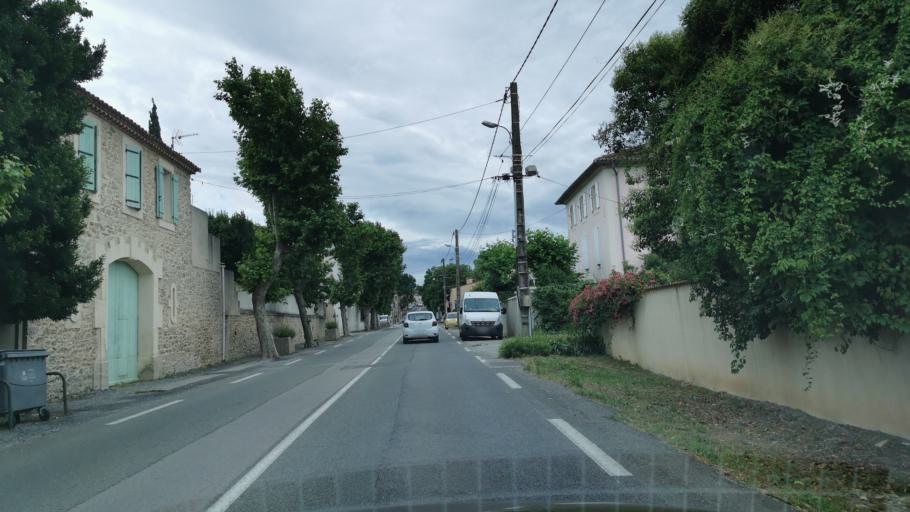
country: FR
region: Languedoc-Roussillon
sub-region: Departement de l'Aude
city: Marcorignan
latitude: 43.2292
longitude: 2.9233
